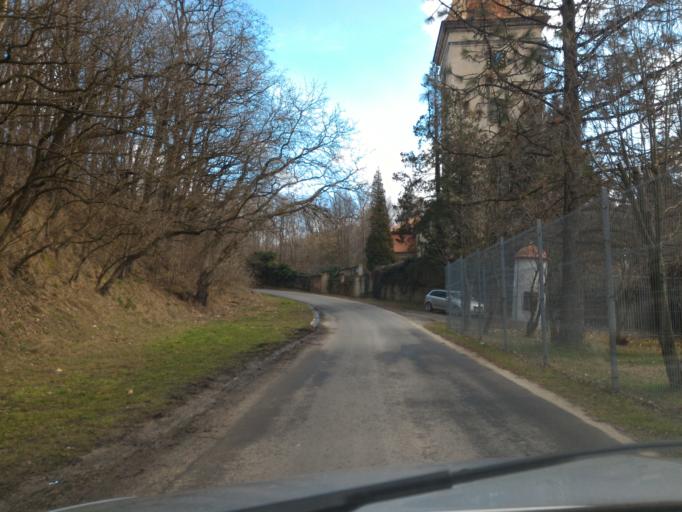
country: DE
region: Saxony
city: Ostritz
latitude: 51.0397
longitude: 14.9866
